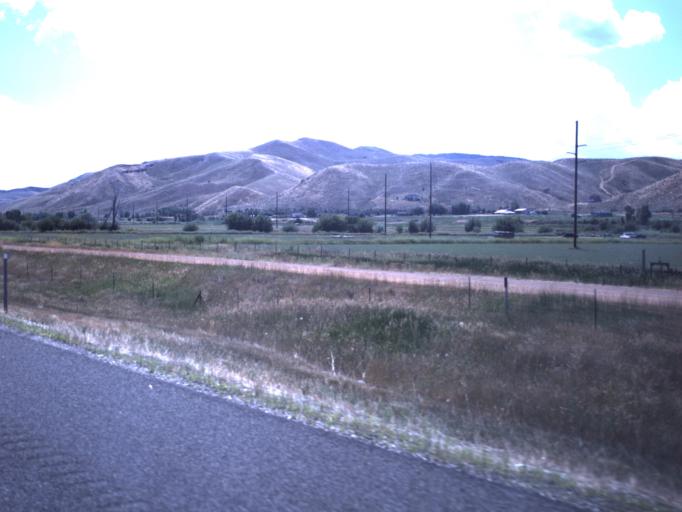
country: US
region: Utah
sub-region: Summit County
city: Coalville
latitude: 41.0099
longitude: -111.4817
